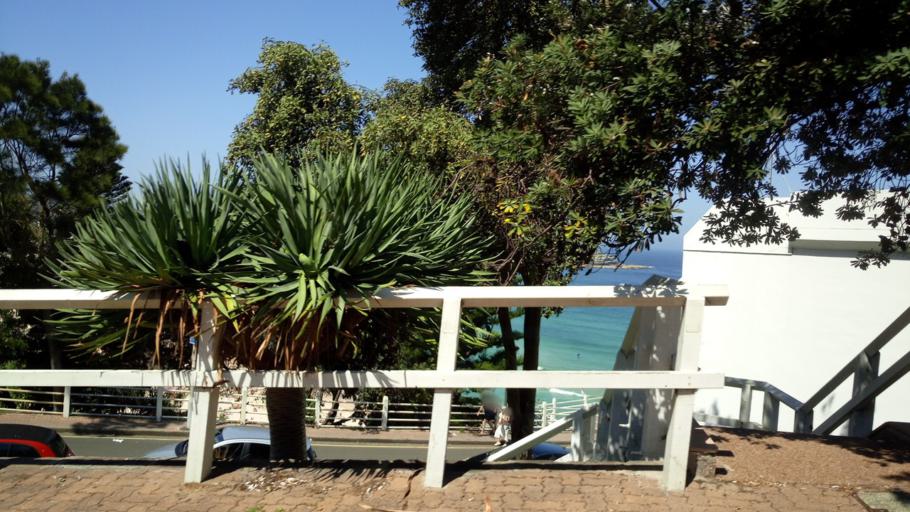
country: AU
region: New South Wales
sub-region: Waverley
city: Bondi Beach
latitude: -33.8942
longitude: 151.2731
